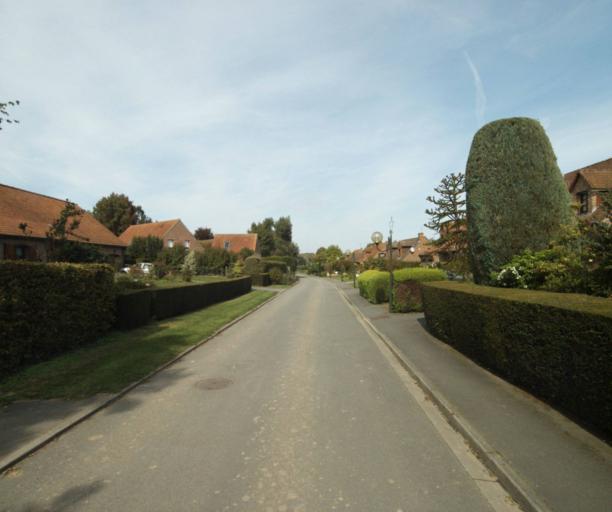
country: FR
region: Nord-Pas-de-Calais
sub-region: Departement du Nord
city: Ennetieres-en-Weppes
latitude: 50.6225
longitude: 2.9298
